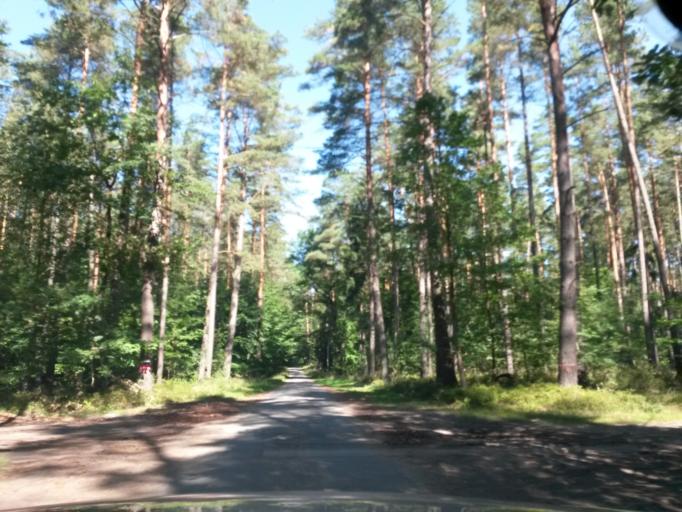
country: DE
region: Brandenburg
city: Templin
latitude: 53.2077
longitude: 13.4539
